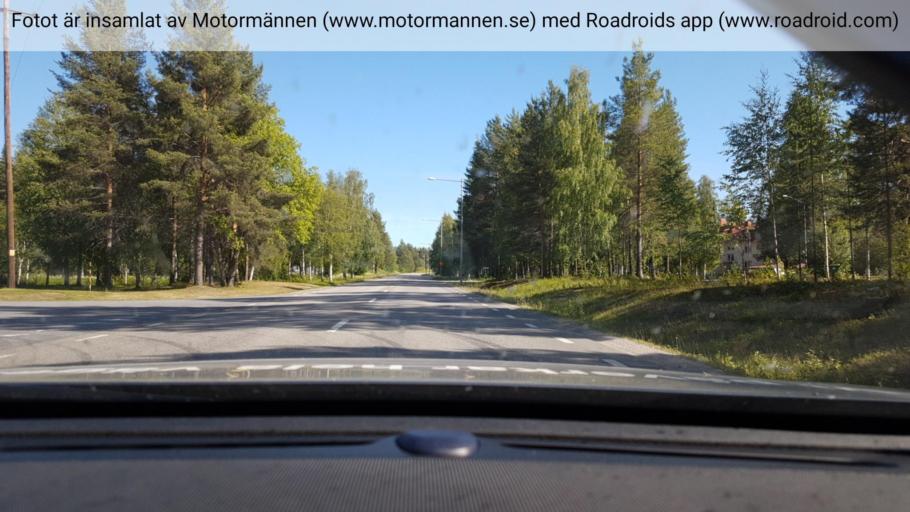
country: SE
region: Vaesterbotten
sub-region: Lycksele Kommun
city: Lycksele
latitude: 64.5817
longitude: 18.7006
